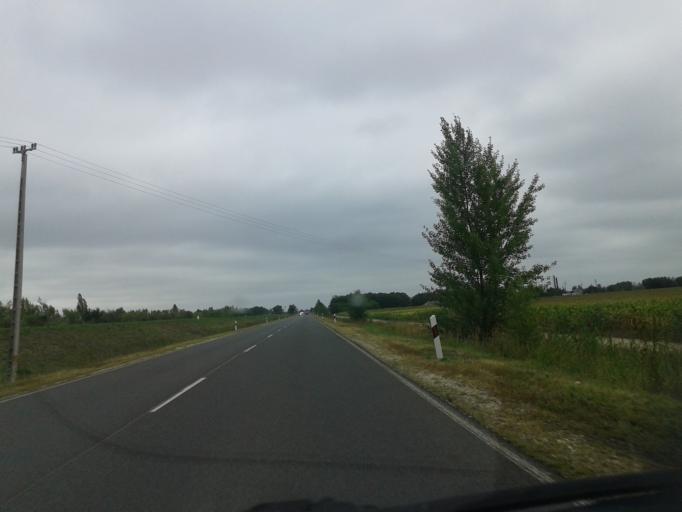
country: HU
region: Bacs-Kiskun
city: Solt
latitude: 46.7747
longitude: 19.0067
